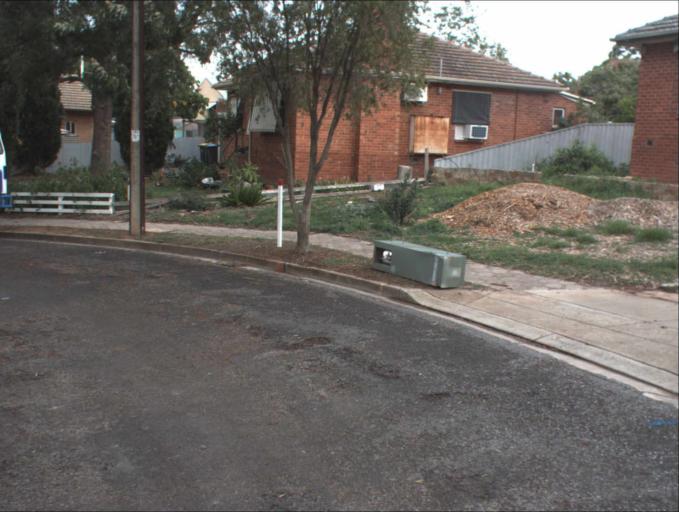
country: AU
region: South Australia
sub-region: Port Adelaide Enfield
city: Klemzig
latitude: -34.8715
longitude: 138.6477
